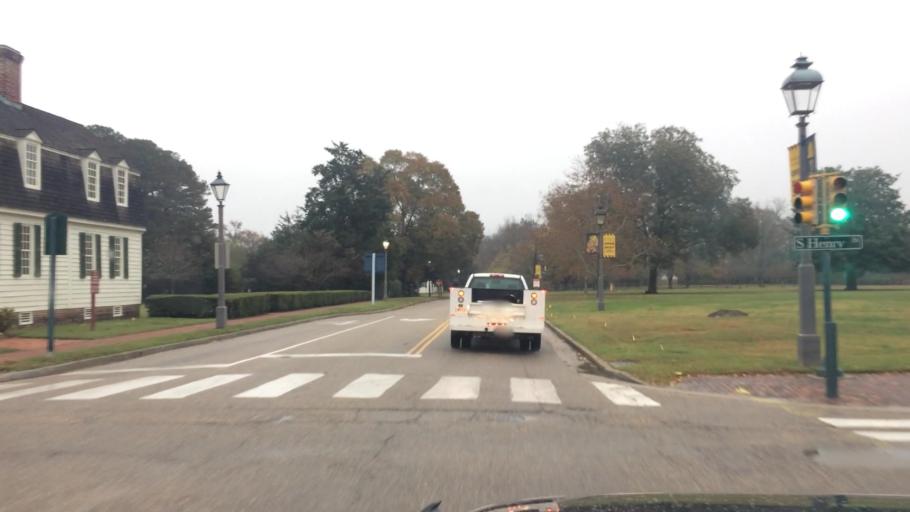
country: US
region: Virginia
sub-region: City of Williamsburg
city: Williamsburg
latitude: 37.2696
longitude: -76.7058
